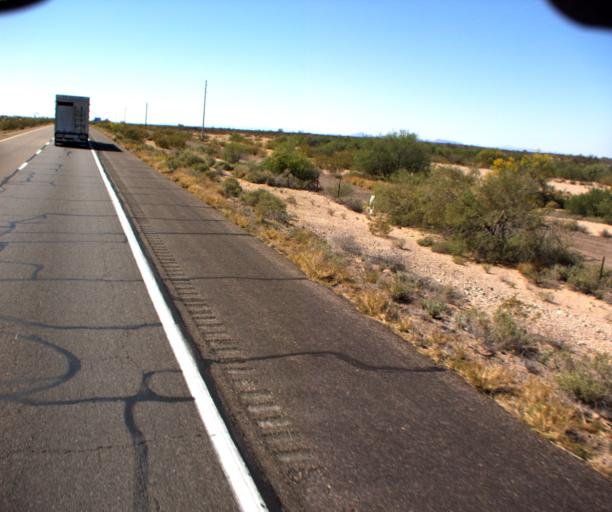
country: US
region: Arizona
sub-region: Maricopa County
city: Gila Bend
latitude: 32.8565
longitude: -113.2368
